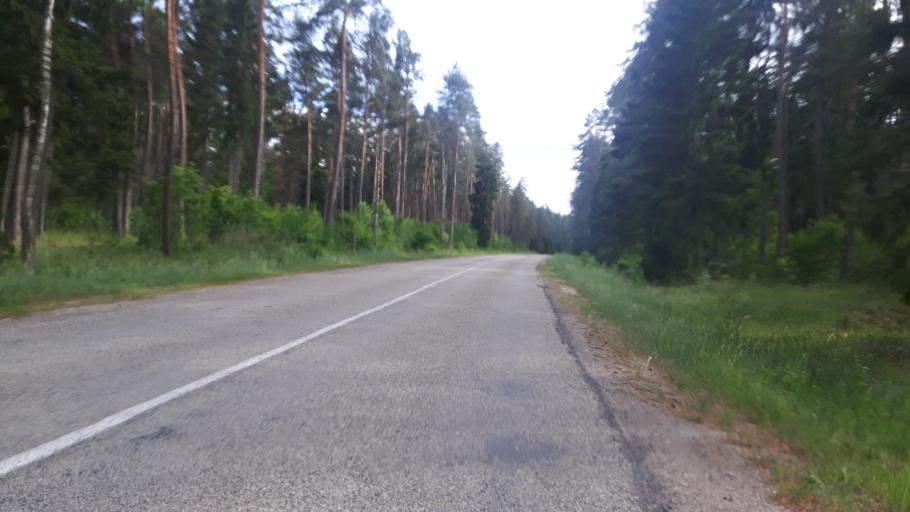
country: LV
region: Engure
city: Smarde
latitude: 57.0053
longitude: 23.3337
